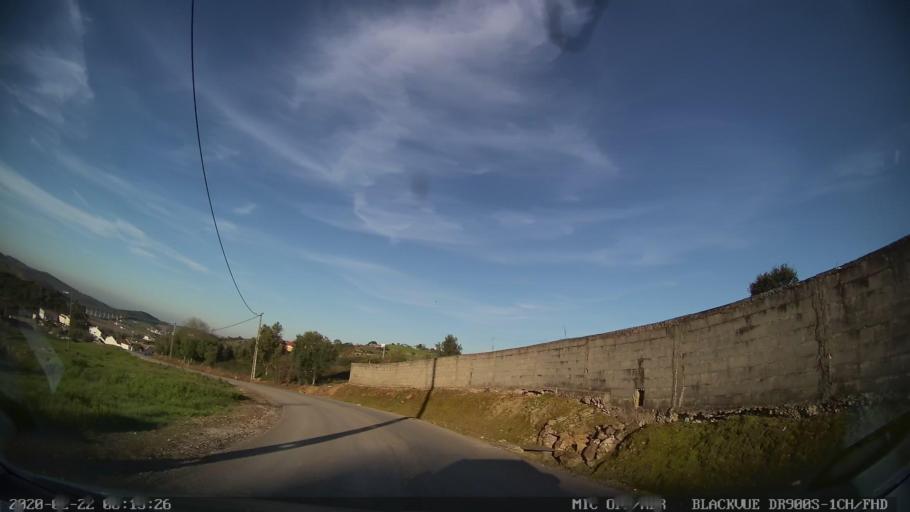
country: PT
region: Lisbon
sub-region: Vila Franca de Xira
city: Vila Franca de Xira
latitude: 38.9857
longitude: -9.0141
